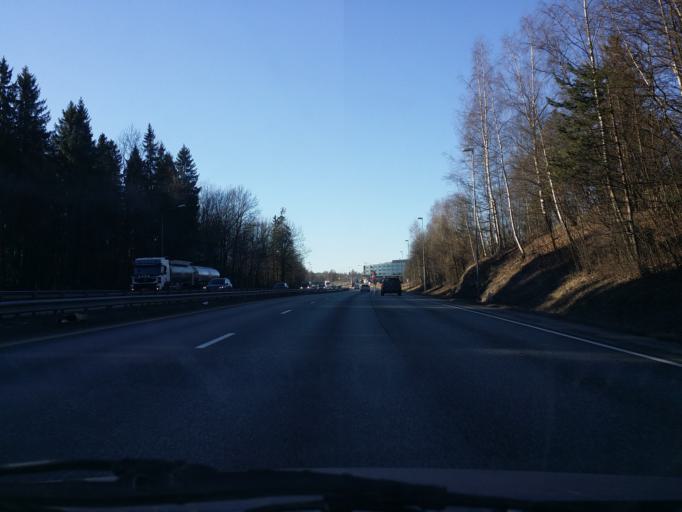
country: NO
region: Akershus
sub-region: Asker
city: Asker
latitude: 59.8377
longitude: 10.4498
